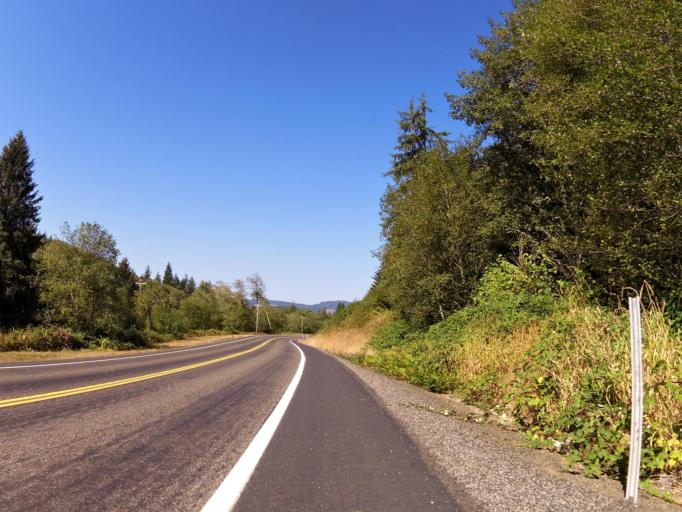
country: US
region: Oregon
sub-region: Tillamook County
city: Tillamook
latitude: 45.3241
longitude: -123.8473
